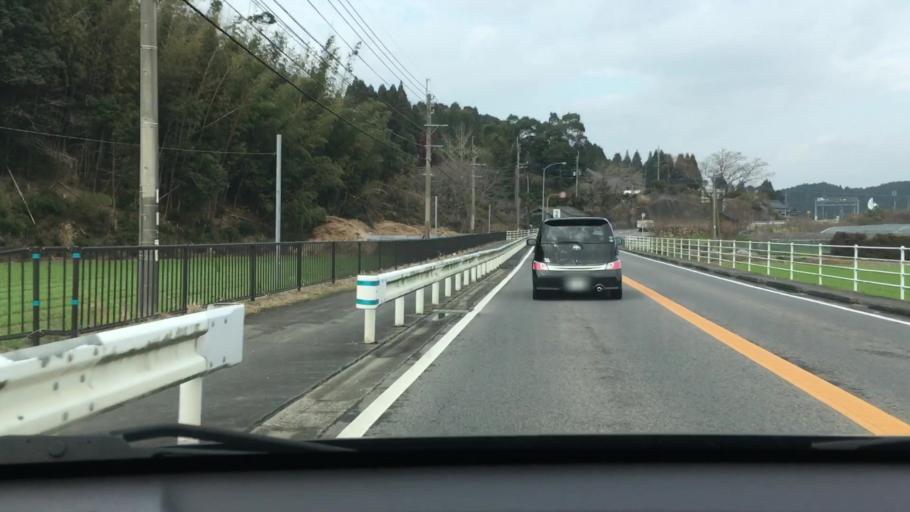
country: JP
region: Saga Prefecture
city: Imaricho-ko
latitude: 33.3290
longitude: 129.9300
